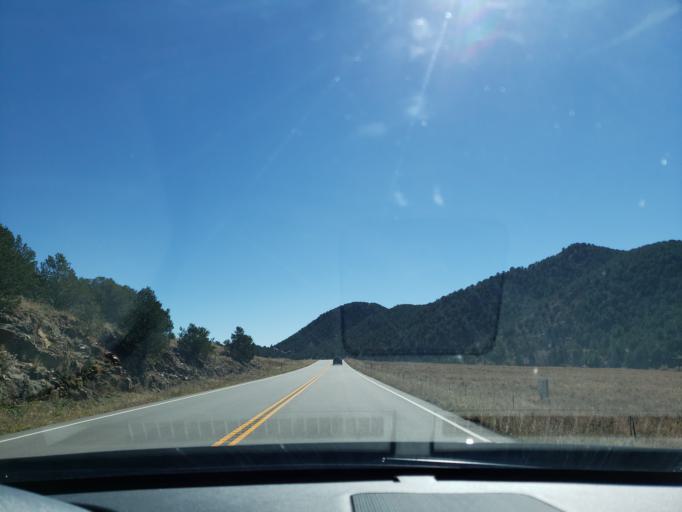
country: US
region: Colorado
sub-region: Fremont County
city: Canon City
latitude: 38.6256
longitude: -105.4575
